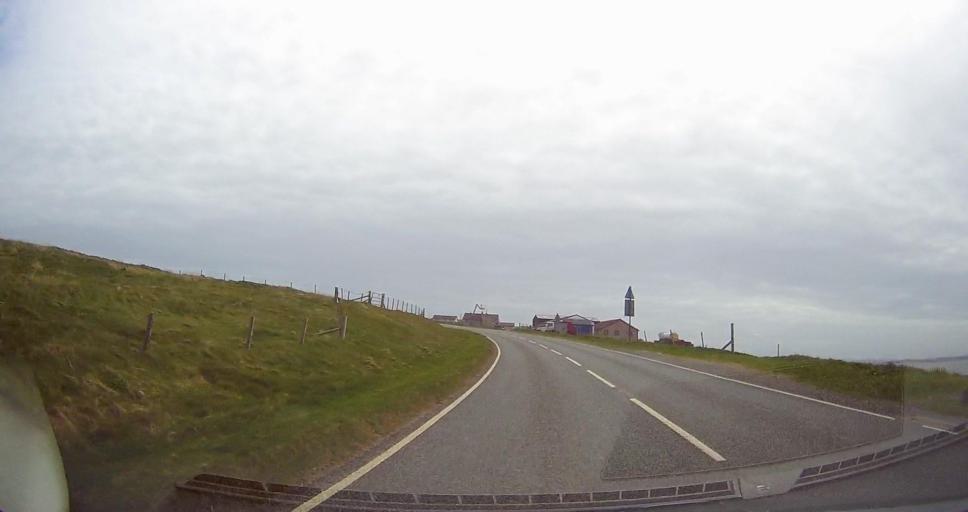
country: GB
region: Scotland
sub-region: Shetland Islands
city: Sandwick
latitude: 59.8788
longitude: -1.3066
